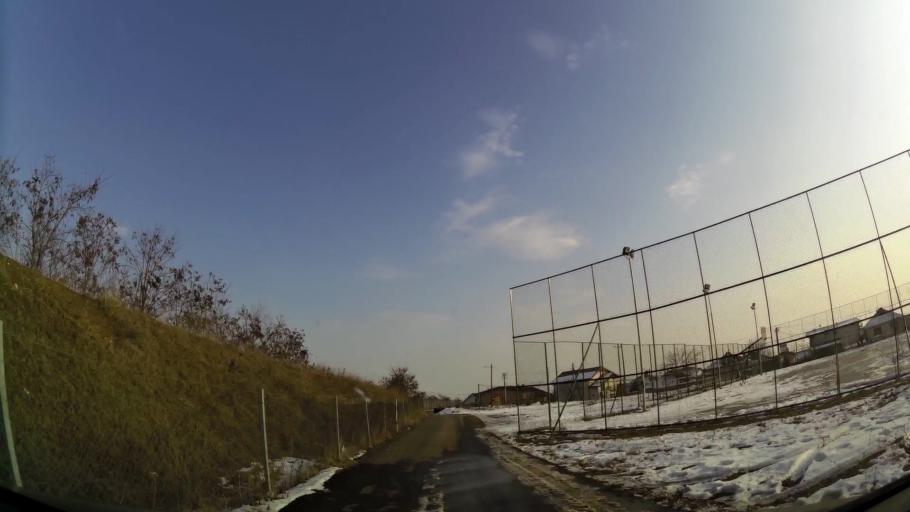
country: MK
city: Creshevo
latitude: 42.0323
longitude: 21.5257
